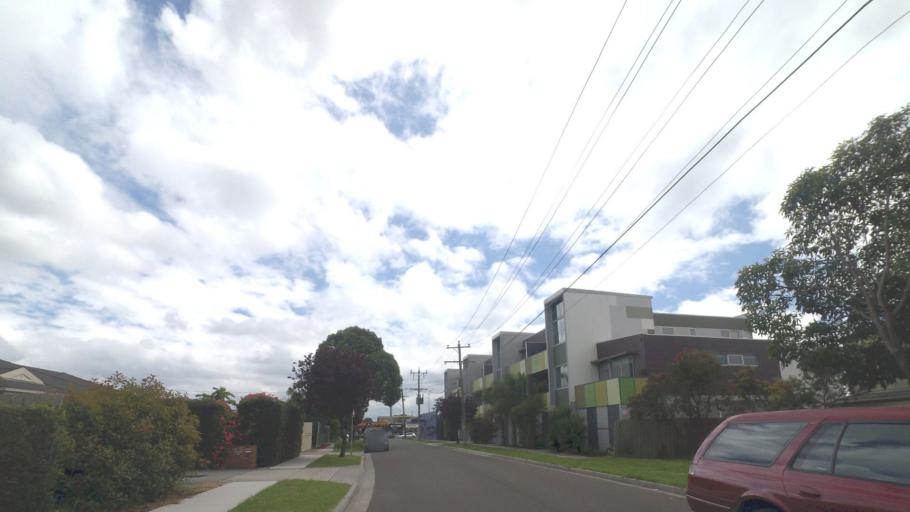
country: AU
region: Victoria
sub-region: Knox
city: Bayswater
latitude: -37.8426
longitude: 145.2643
